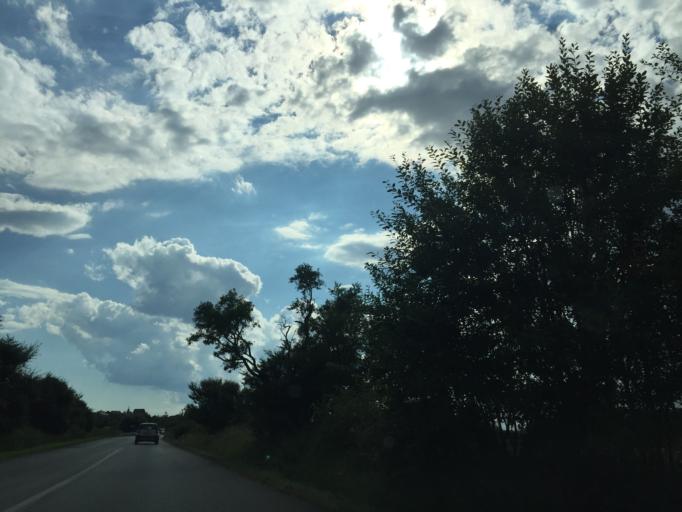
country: SK
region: Zilinsky
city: Namestovo
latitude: 49.3920
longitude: 19.4743
